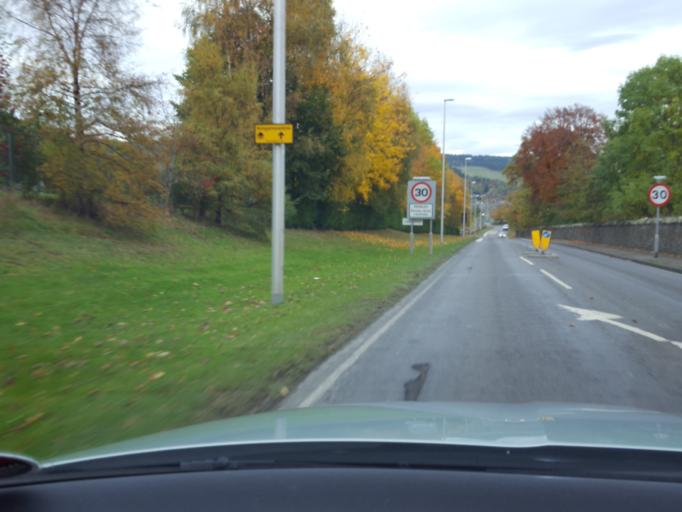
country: GB
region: Scotland
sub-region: The Scottish Borders
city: Peebles
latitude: 55.6527
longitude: -3.2062
